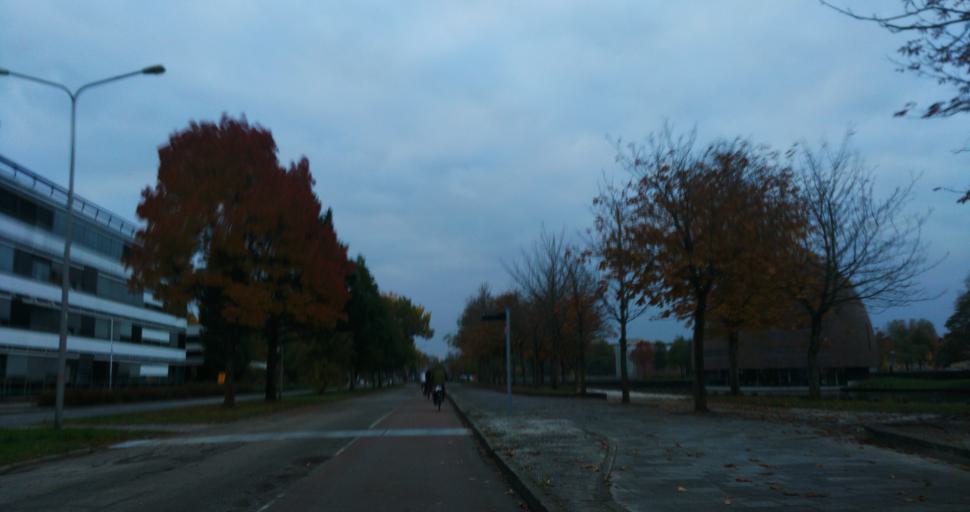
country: NL
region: Groningen
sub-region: Gemeente Groningen
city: Korrewegwijk
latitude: 53.2397
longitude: 6.5360
